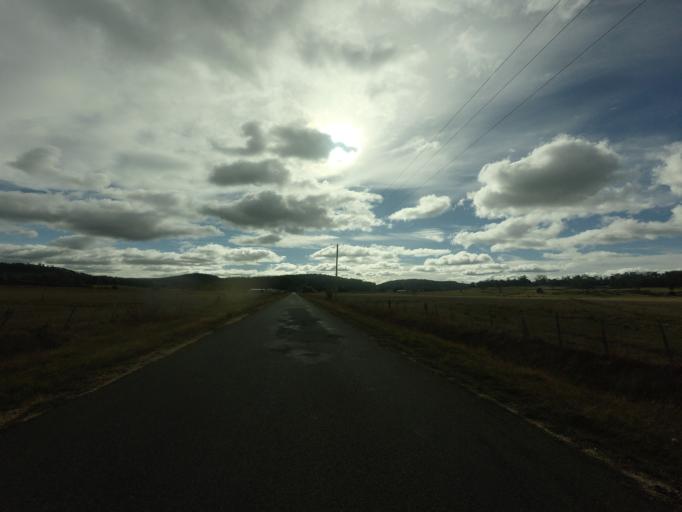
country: AU
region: Tasmania
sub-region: Brighton
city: Bridgewater
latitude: -42.4058
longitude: 147.3945
